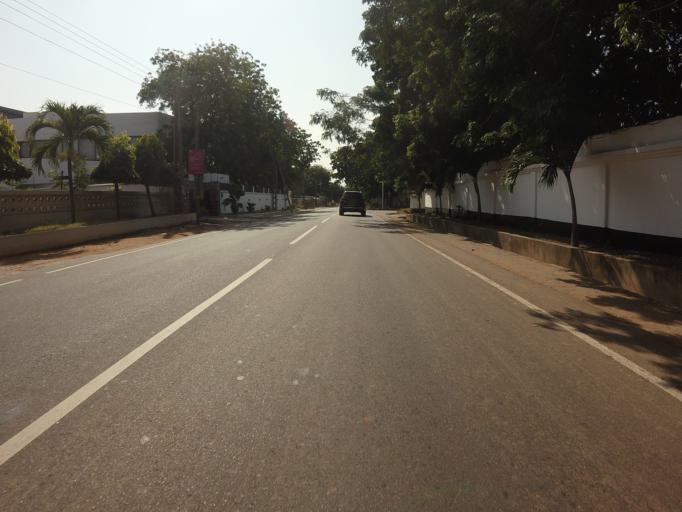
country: GH
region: Greater Accra
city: Accra
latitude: 5.5777
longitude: -0.1670
